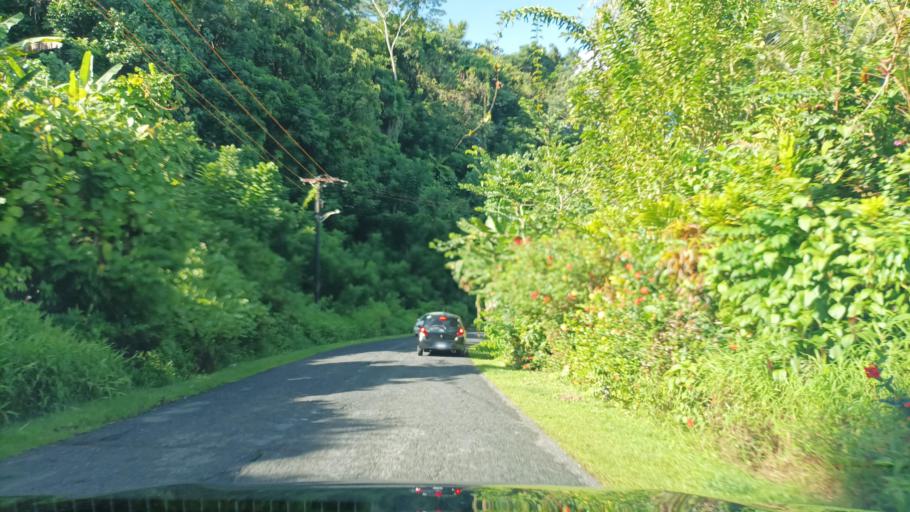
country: FM
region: Pohnpei
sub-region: Kolonia Municipality
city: Kolonia Town
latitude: 6.9481
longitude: 158.1873
